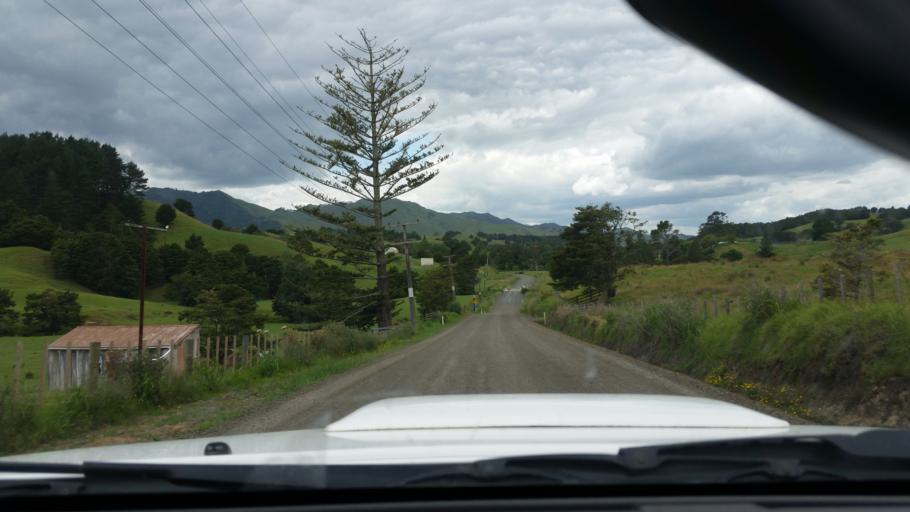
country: NZ
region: Northland
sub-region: Kaipara District
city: Dargaville
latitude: -35.8125
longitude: 173.8887
